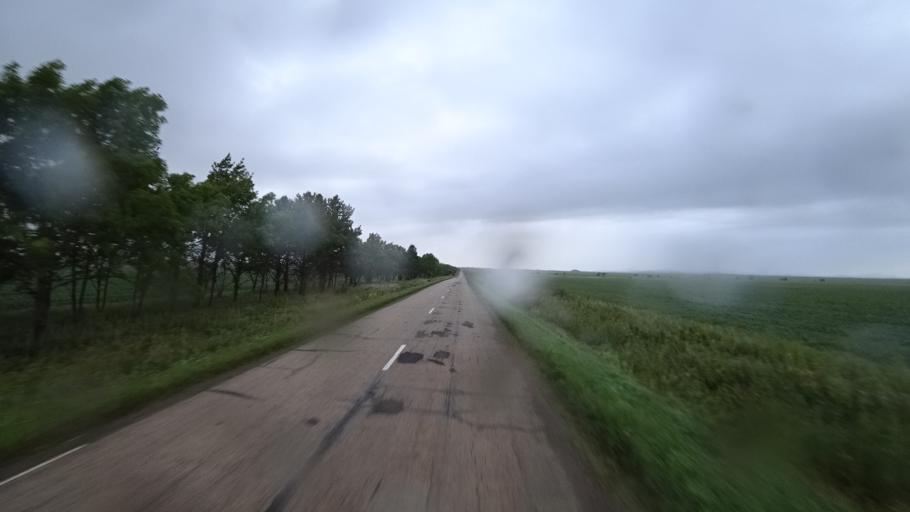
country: RU
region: Primorskiy
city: Chernigovka
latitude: 44.3744
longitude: 132.5298
